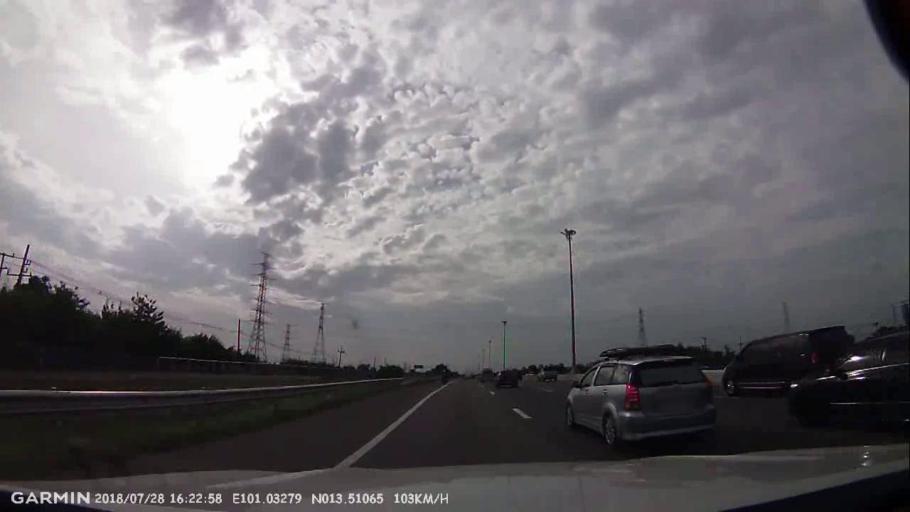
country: TH
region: Chachoengsao
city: Bang Pakong
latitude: 13.5108
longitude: 101.0326
